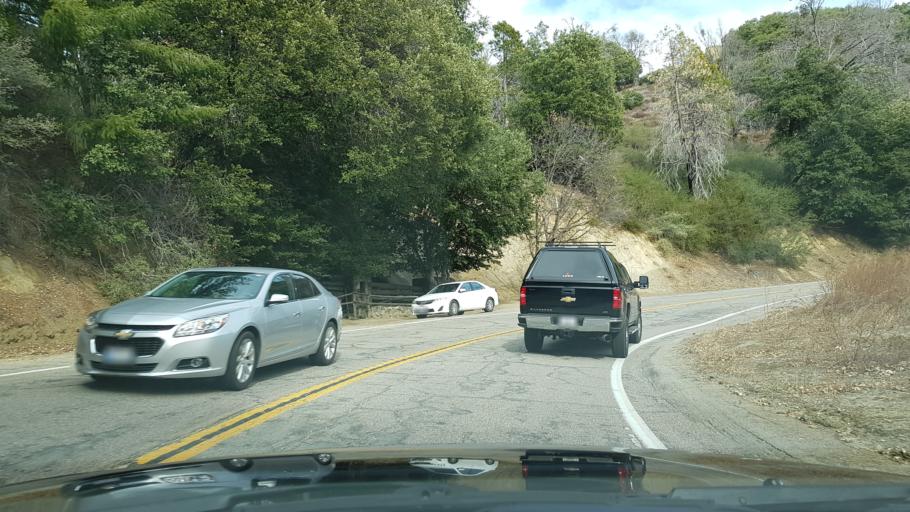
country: US
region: California
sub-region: Riverside County
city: Aguanga
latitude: 33.3141
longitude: -116.8710
